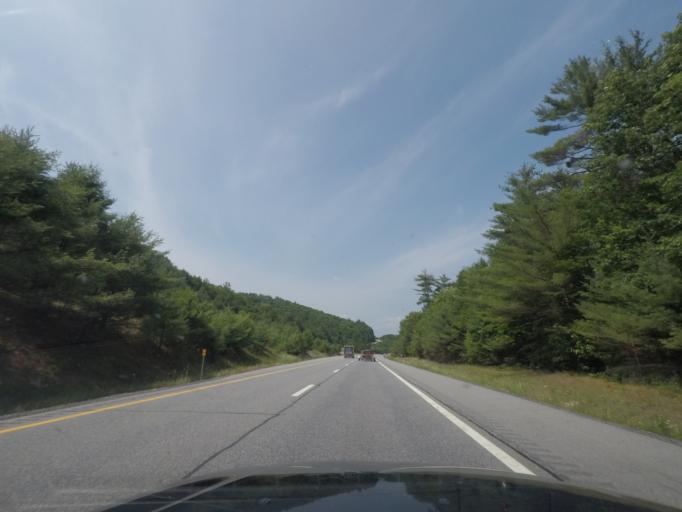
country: US
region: New York
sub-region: Warren County
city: Warrensburg
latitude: 43.6259
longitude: -73.7496
